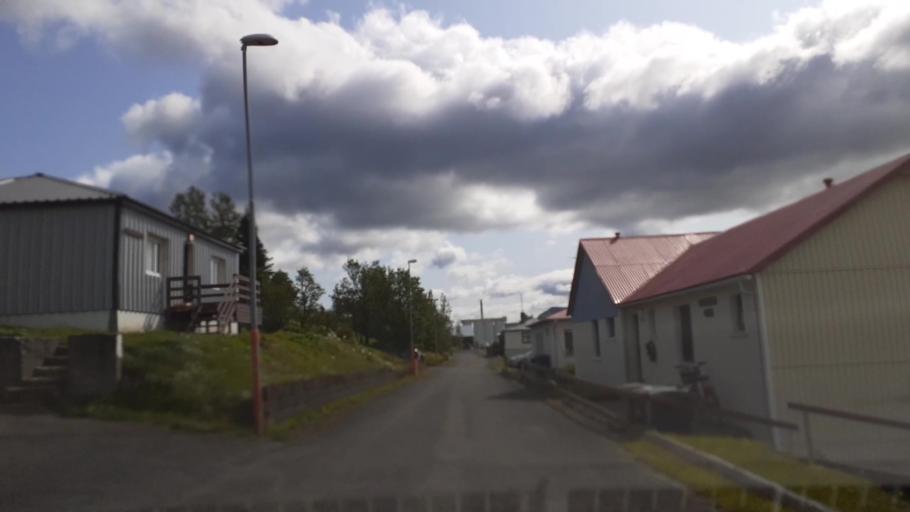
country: IS
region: East
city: Eskifjoerdur
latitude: 64.9272
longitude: -14.0017
